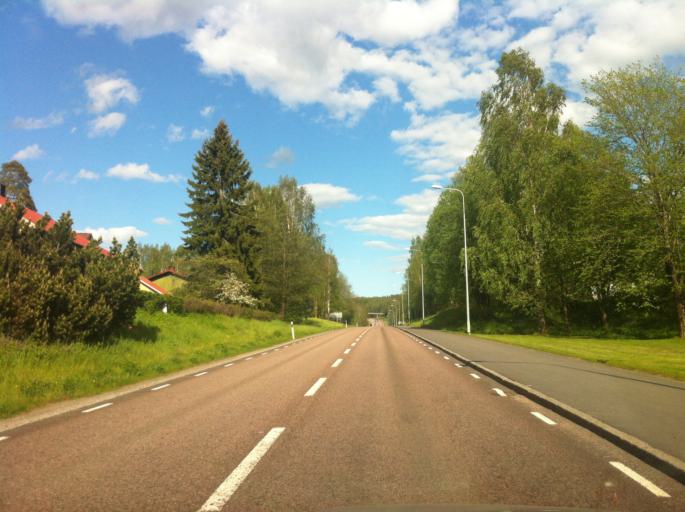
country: SE
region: Vaermland
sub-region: Filipstads Kommun
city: Filipstad
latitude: 59.7098
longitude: 14.1794
